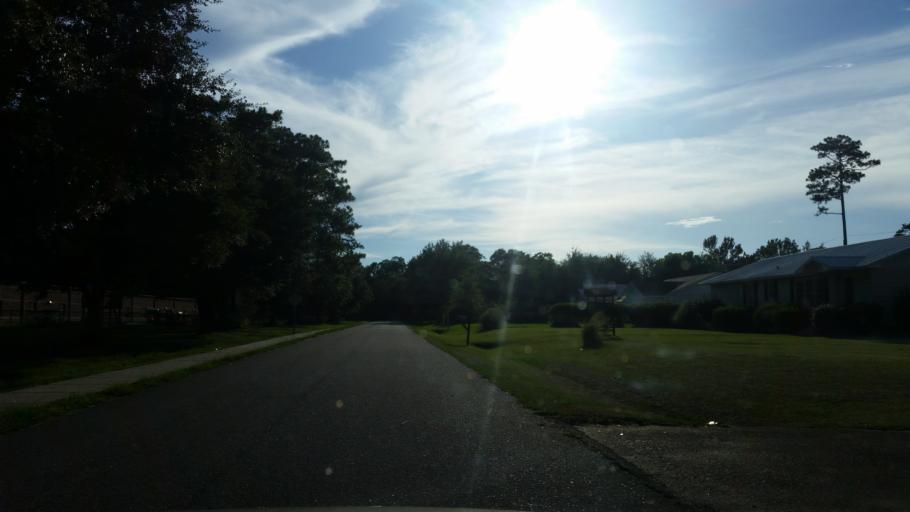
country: US
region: Alabama
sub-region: Baldwin County
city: Foley
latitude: 30.4107
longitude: -87.6896
